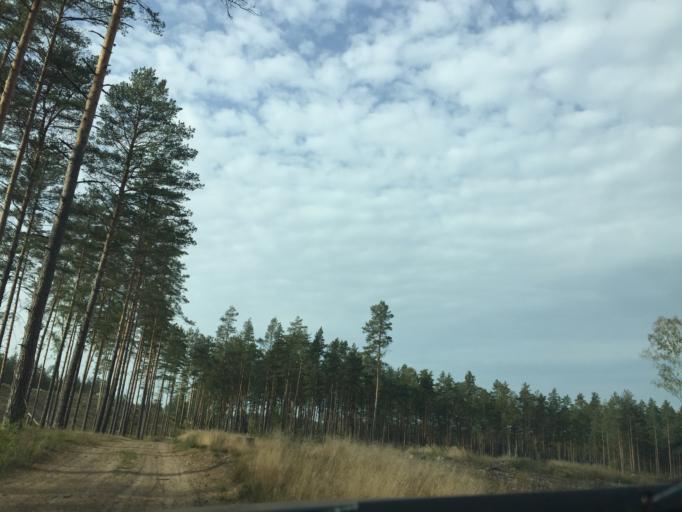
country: LV
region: Garkalne
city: Garkalne
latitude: 56.9540
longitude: 24.4231
